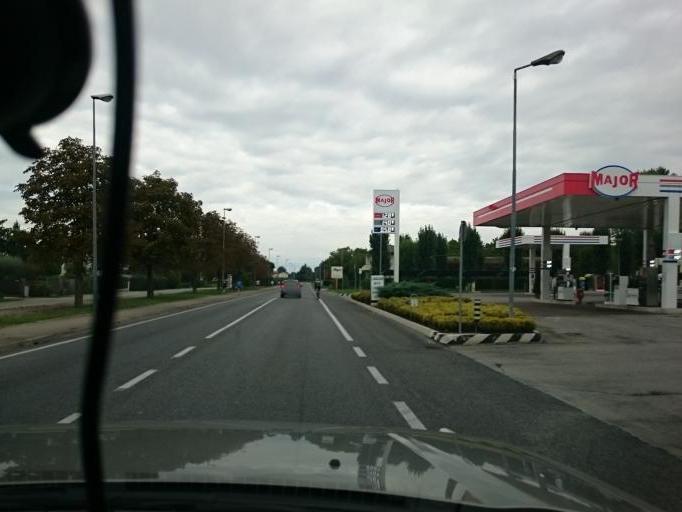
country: IT
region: Veneto
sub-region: Provincia di Padova
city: Saccolongo
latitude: 45.3970
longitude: 11.7628
